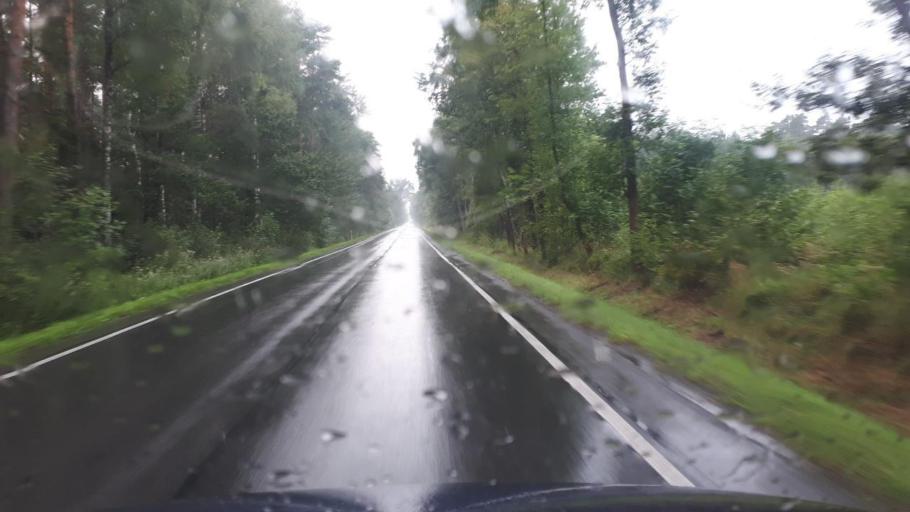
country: PL
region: Silesian Voivodeship
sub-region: Powiat tarnogorski
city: Tworog
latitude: 50.5297
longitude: 18.6759
